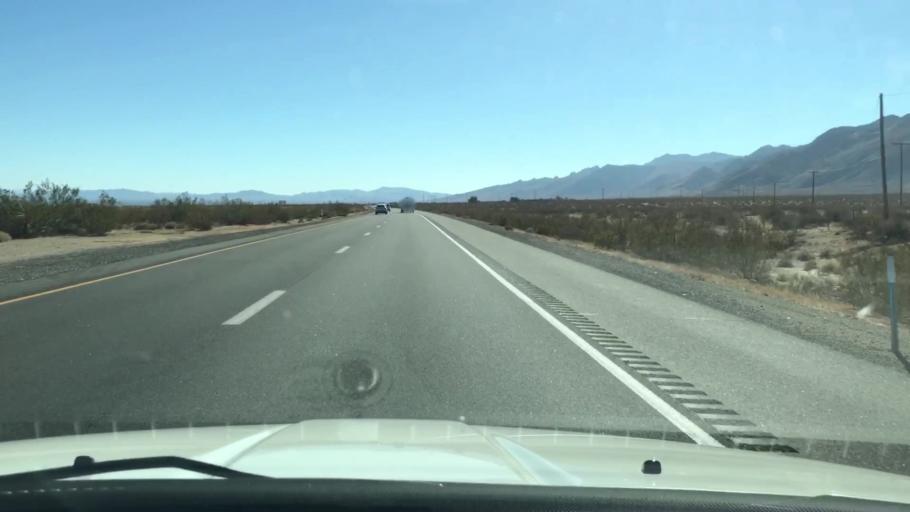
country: US
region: California
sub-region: Kern County
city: Inyokern
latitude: 35.8497
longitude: -117.8759
